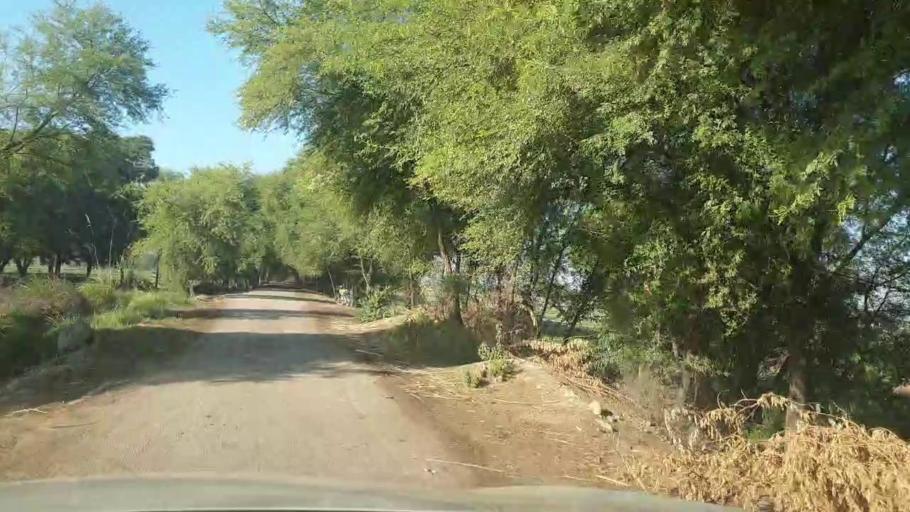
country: PK
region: Sindh
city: Bhan
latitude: 26.5518
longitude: 67.6839
